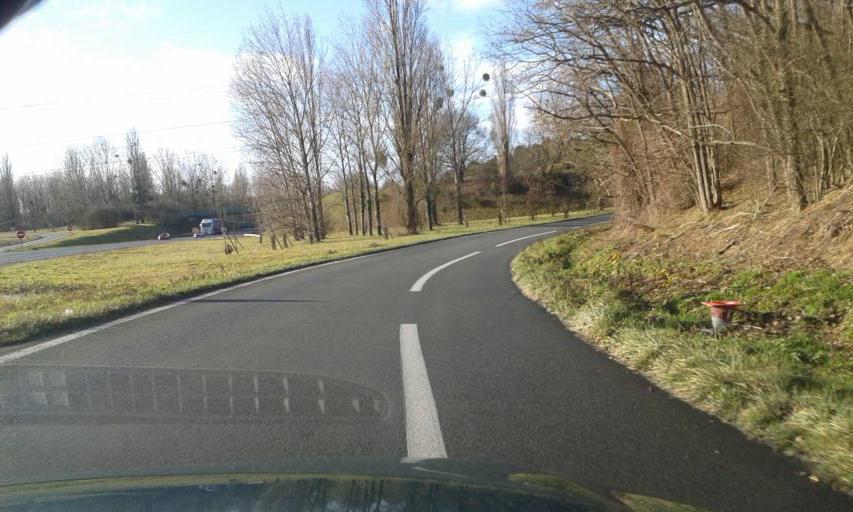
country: FR
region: Picardie
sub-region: Departement de l'Oise
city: Remy
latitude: 49.4010
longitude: 2.7031
